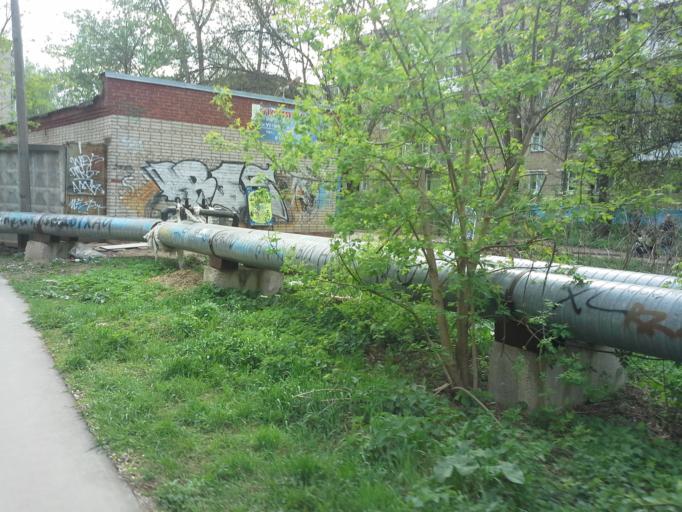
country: RU
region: Moskovskaya
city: Sergiyev Posad
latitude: 56.3191
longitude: 38.1438
